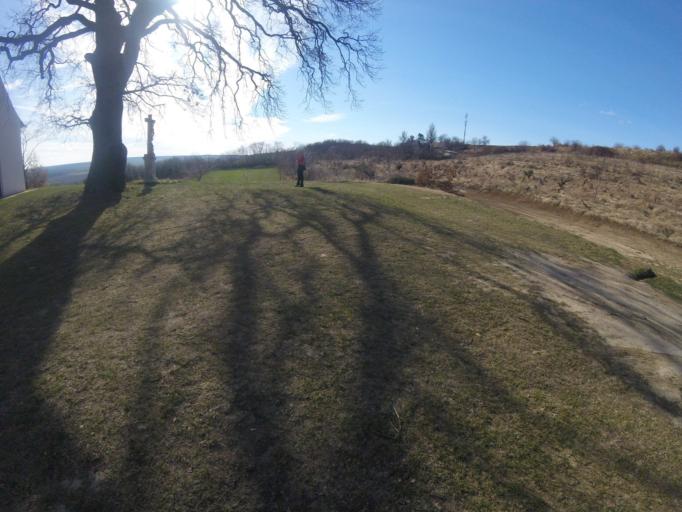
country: HU
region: Tolna
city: Bataszek
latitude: 46.1701
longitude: 18.7001
